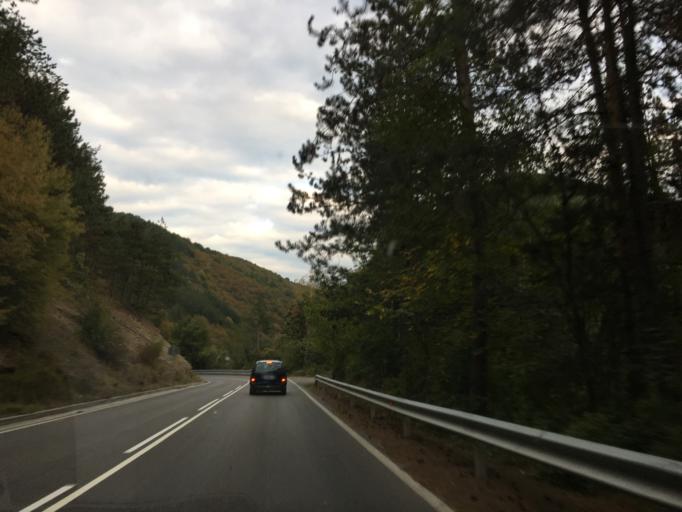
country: BG
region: Sofiya
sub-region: Obshtina Svoge
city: Svoge
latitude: 42.9360
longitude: 23.3859
